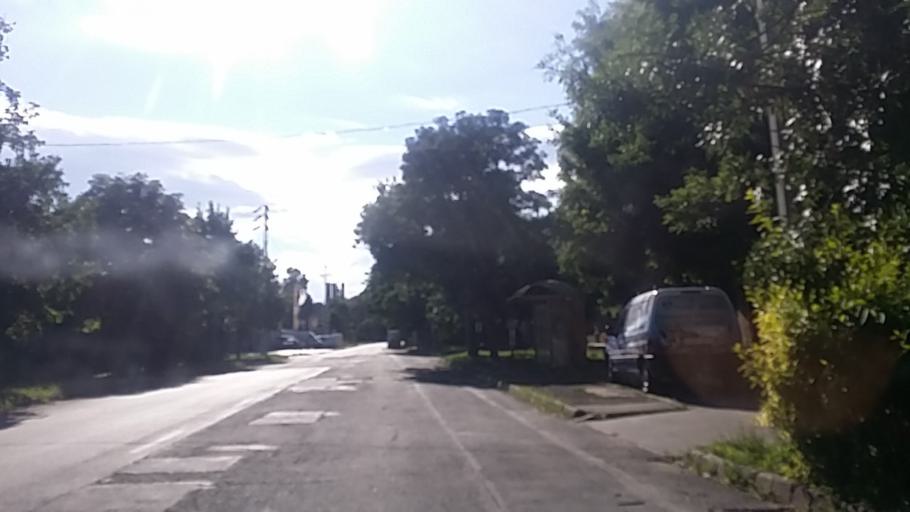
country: HU
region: Pest
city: Vac
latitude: 47.7752
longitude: 19.1425
